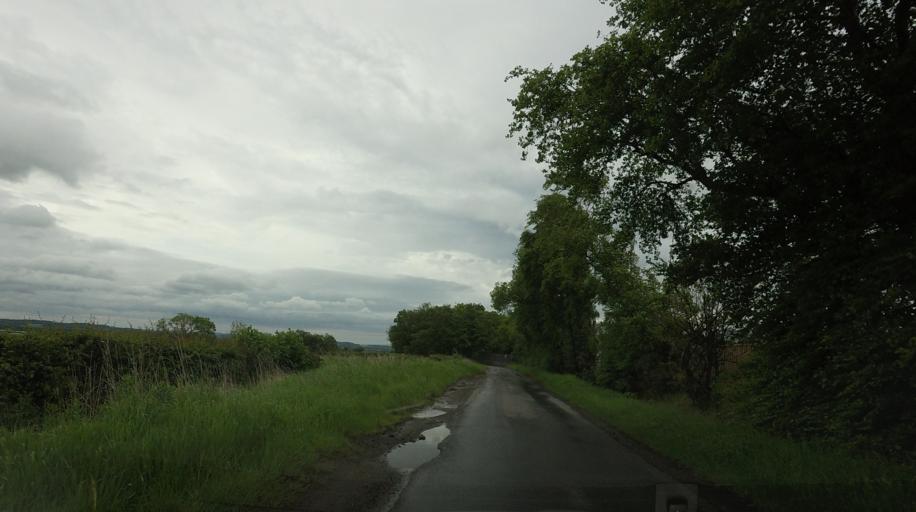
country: GB
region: Scotland
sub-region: West Lothian
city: Broxburn
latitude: 55.9194
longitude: -3.4562
